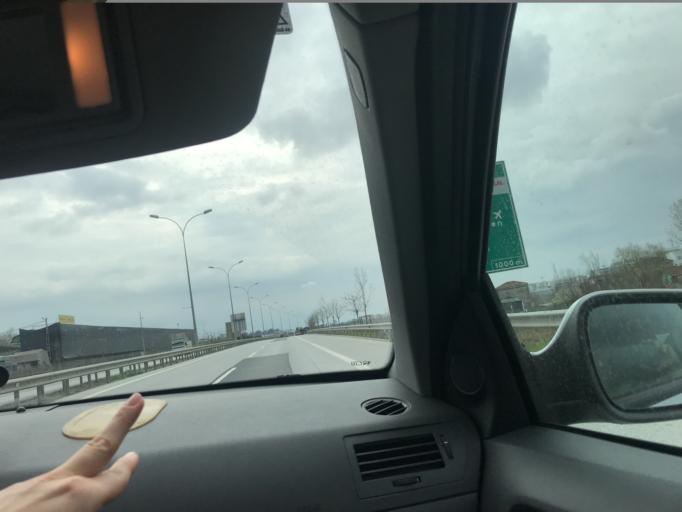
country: TR
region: Istanbul
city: Sultanbeyli
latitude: 40.9272
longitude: 29.3264
